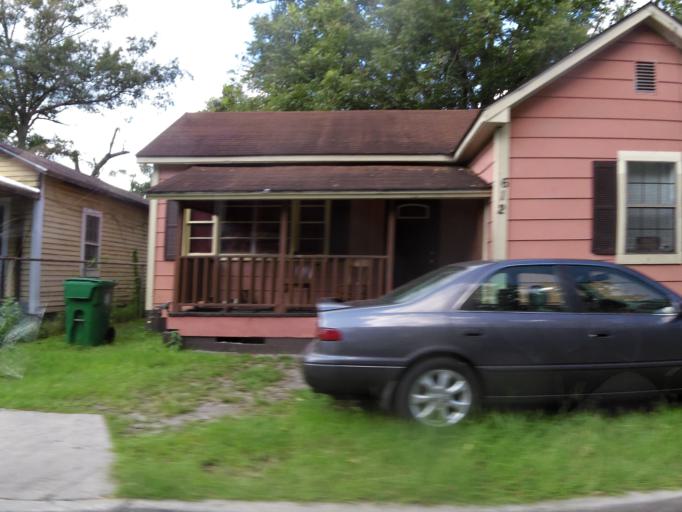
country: US
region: Georgia
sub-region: Lowndes County
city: Valdosta
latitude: 30.8286
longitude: -83.2685
